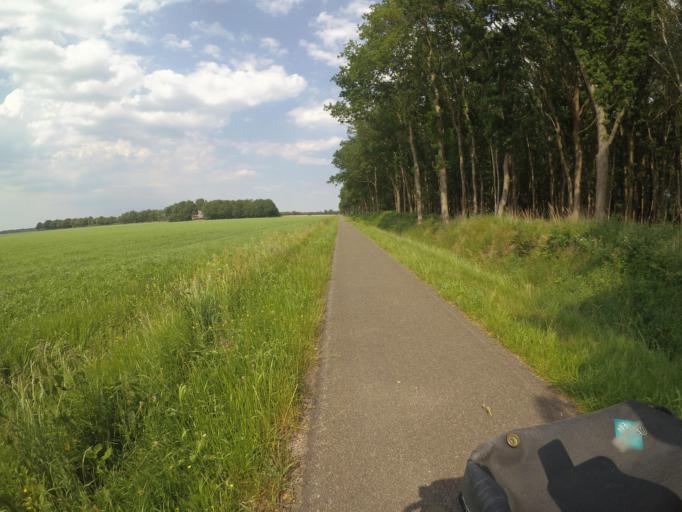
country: NL
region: Drenthe
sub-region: Gemeente Assen
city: Assen
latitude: 52.9564
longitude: 6.4910
